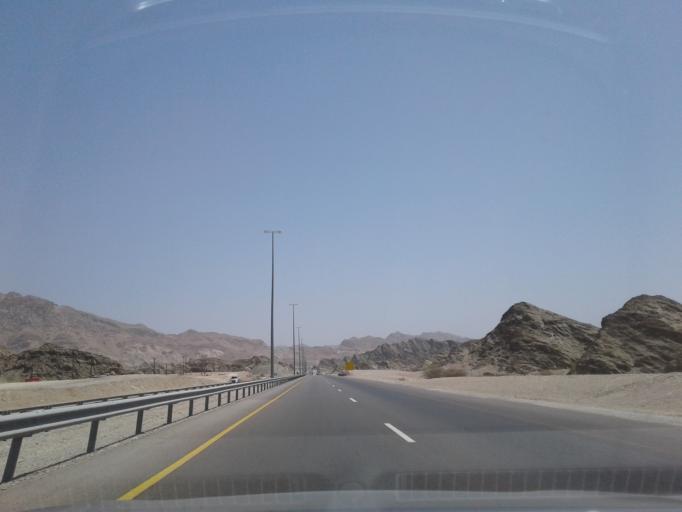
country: OM
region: Muhafazat Masqat
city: Bawshar
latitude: 23.4632
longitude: 58.4957
